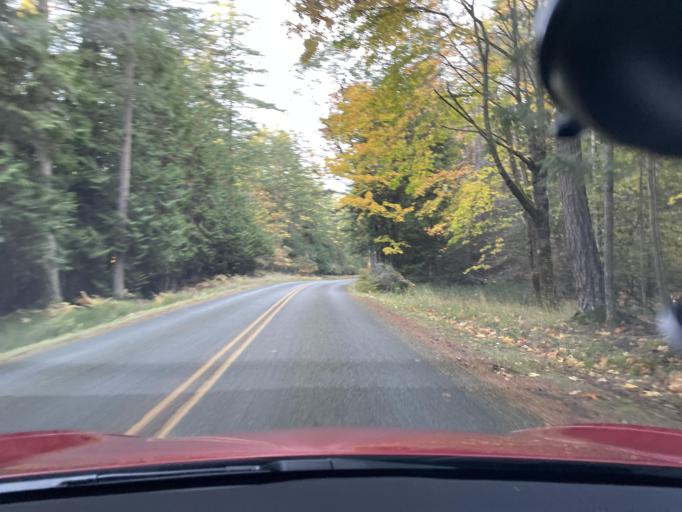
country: US
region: Washington
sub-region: San Juan County
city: Friday Harbor
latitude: 48.5317
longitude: -123.1575
